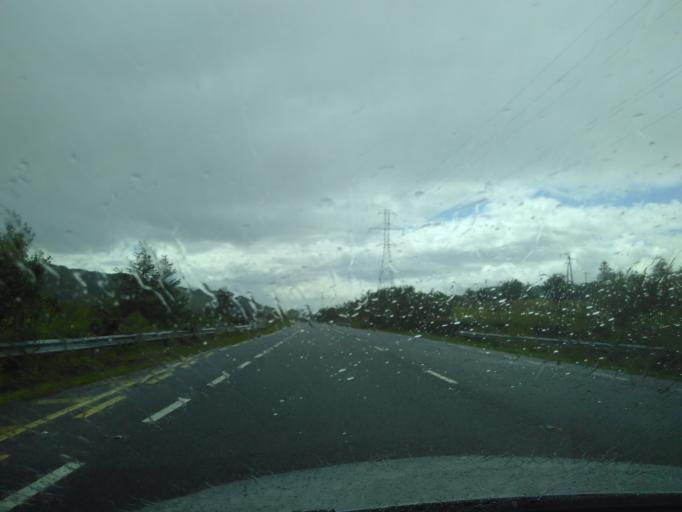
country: IE
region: Ulster
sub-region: County Donegal
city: Donegal
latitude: 54.7111
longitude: -7.9690
